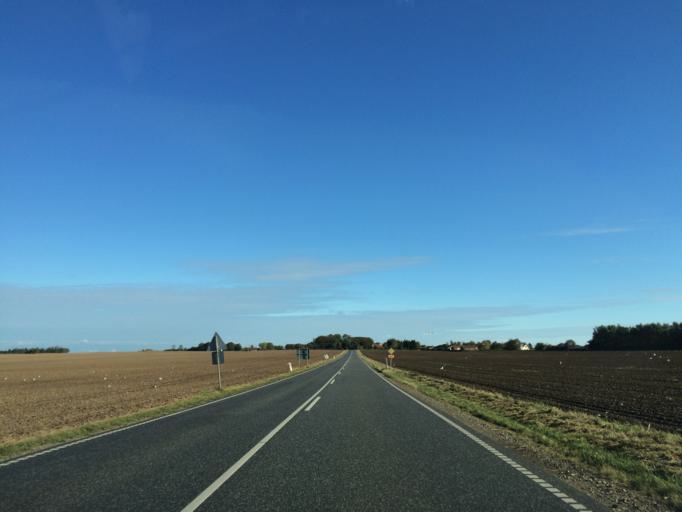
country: DK
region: Central Jutland
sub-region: Randers Kommune
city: Langa
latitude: 56.3385
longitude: 9.8635
